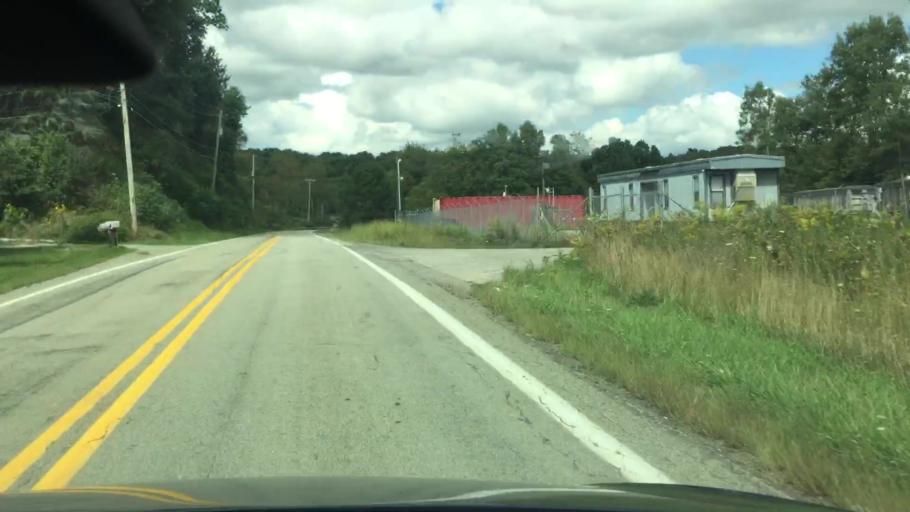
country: US
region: Pennsylvania
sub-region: Allegheny County
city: Curtisville
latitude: 40.6620
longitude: -79.8356
